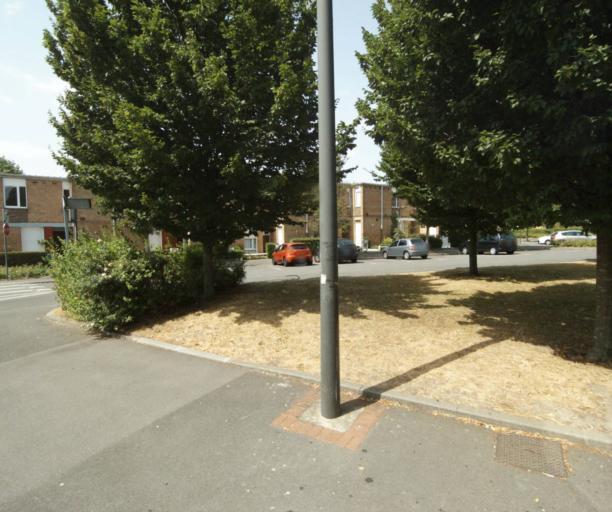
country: FR
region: Nord-Pas-de-Calais
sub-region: Departement du Nord
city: Wattrelos
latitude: 50.7051
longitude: 3.2307
